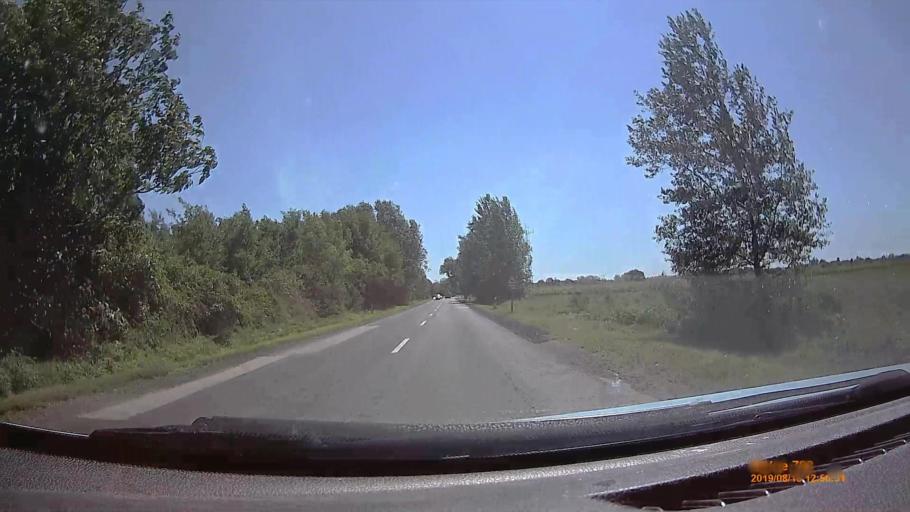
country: HU
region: Fejer
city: Sarkeresztur
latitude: 47.0202
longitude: 18.5437
